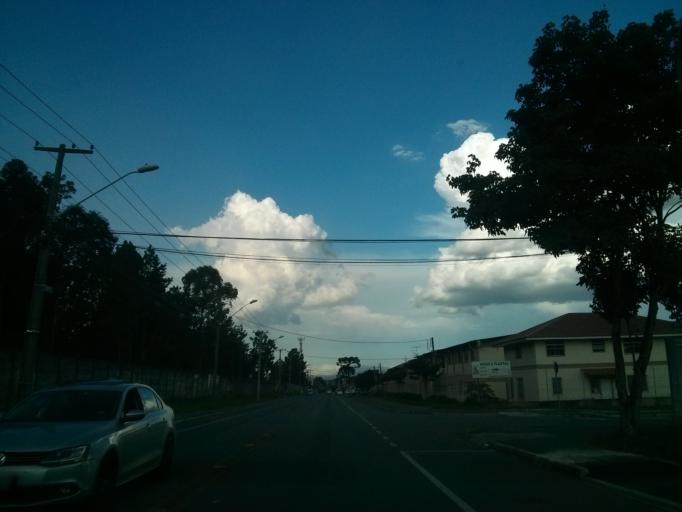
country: BR
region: Parana
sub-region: Sao Jose Dos Pinhais
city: Sao Jose dos Pinhais
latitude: -25.5119
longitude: -49.2367
